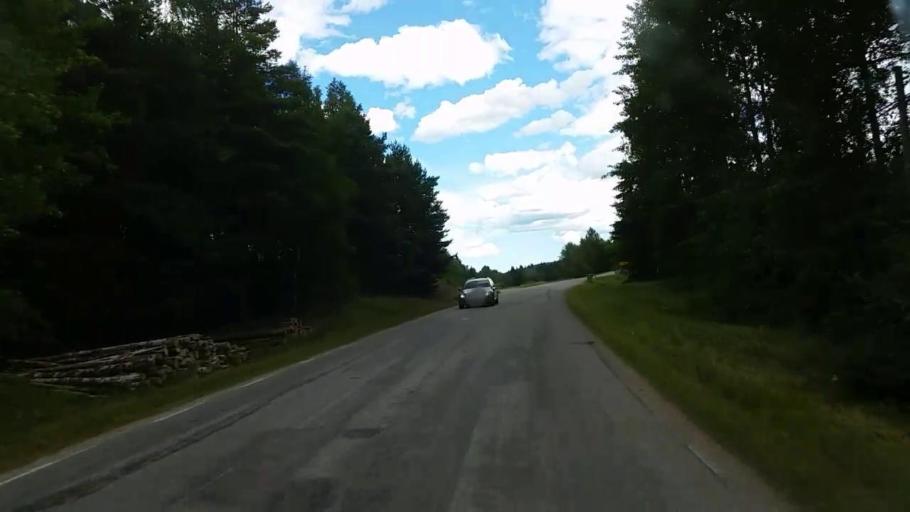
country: SE
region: Gaevleborg
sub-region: Ljusdals Kommun
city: Jaervsoe
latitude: 61.6719
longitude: 16.1183
